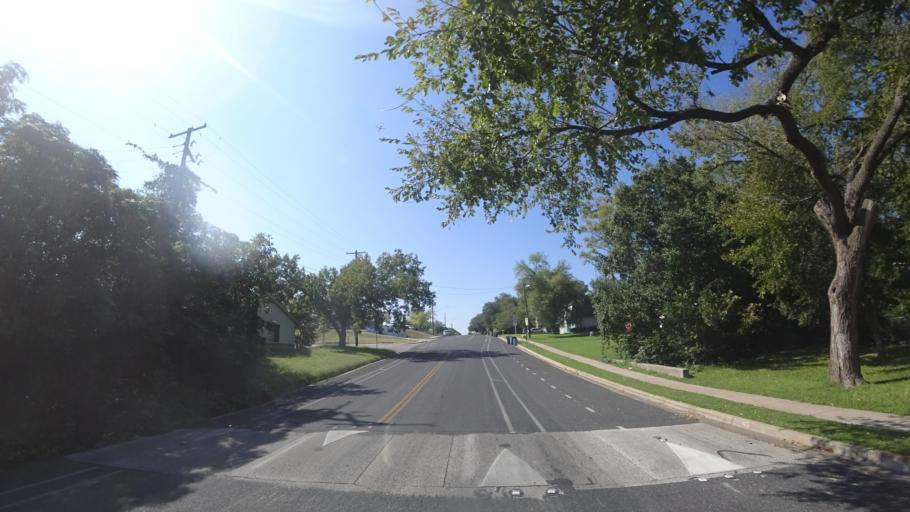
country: US
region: Texas
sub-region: Travis County
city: Austin
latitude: 30.3191
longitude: -97.6798
